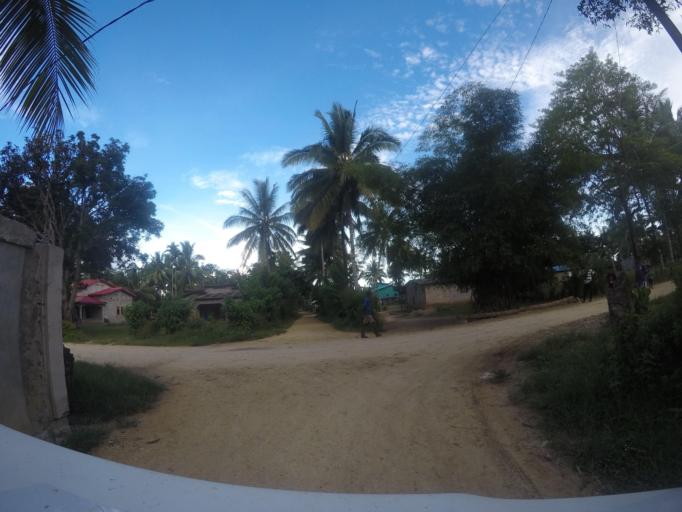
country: TL
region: Lautem
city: Lospalos
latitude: -8.5040
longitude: 126.9951
